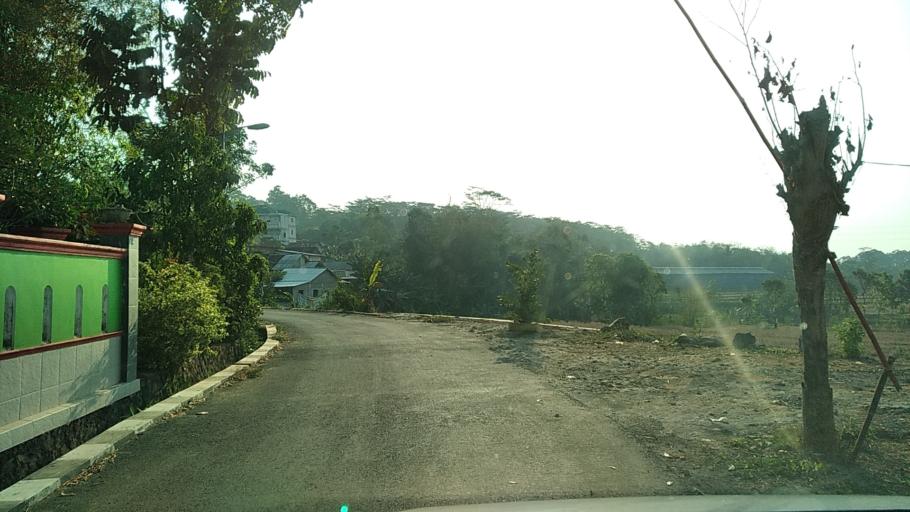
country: ID
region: Central Java
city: Ungaran
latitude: -7.0899
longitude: 110.3590
